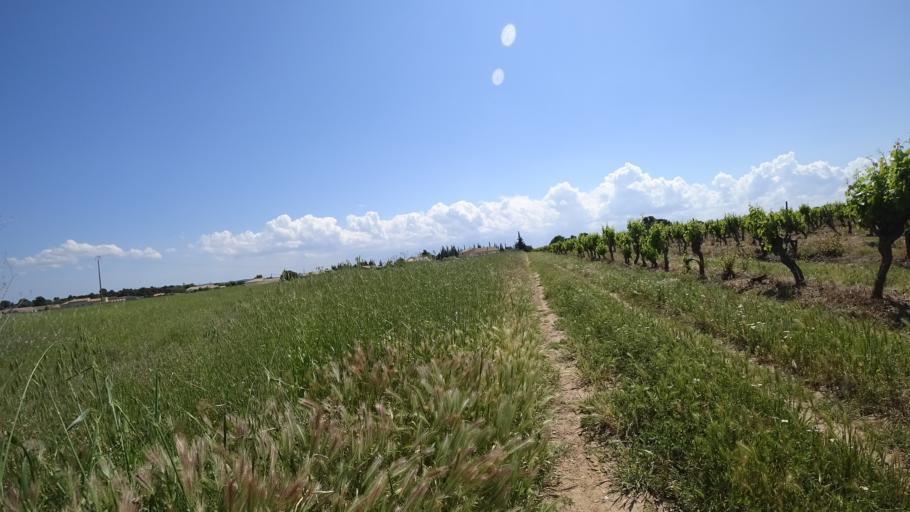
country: FR
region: Languedoc-Roussillon
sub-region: Departement de l'Aude
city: Canet
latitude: 43.2549
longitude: 2.8232
